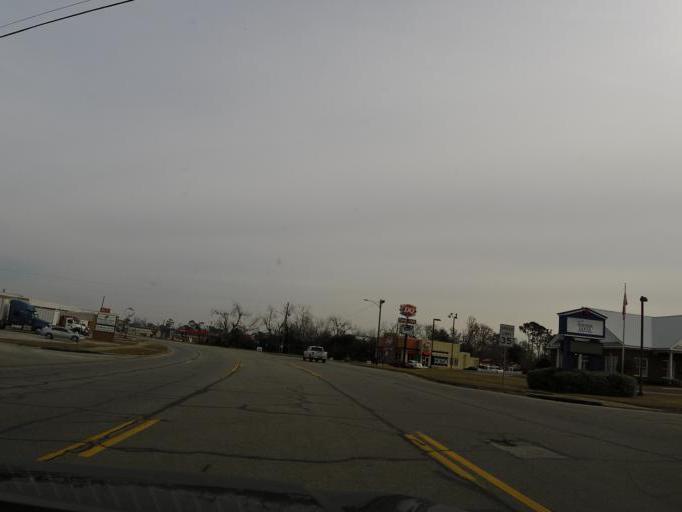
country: US
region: Georgia
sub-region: Seminole County
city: Donalsonville
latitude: 31.0407
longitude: -84.8870
